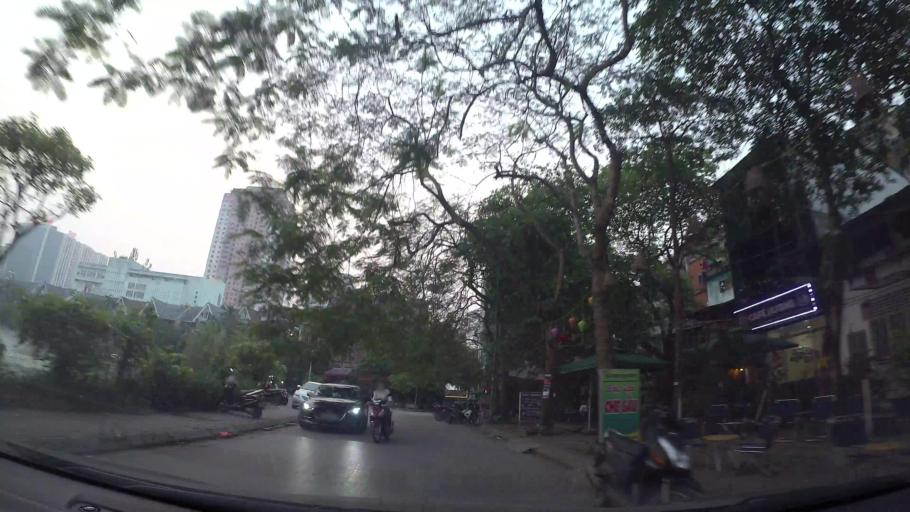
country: VN
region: Ha Noi
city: Ha Dong
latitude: 20.9790
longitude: 105.7910
